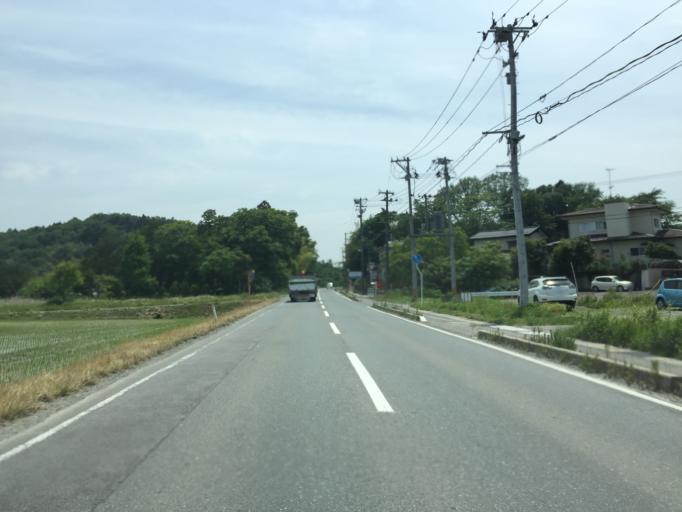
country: JP
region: Fukushima
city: Namie
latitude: 37.6484
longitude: 140.9328
